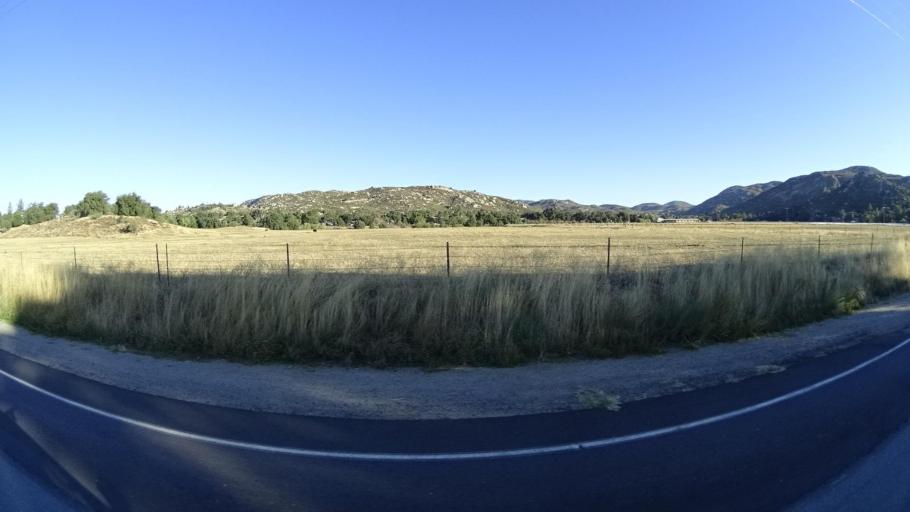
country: US
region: California
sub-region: San Diego County
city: Descanso
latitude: 32.8545
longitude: -116.6001
